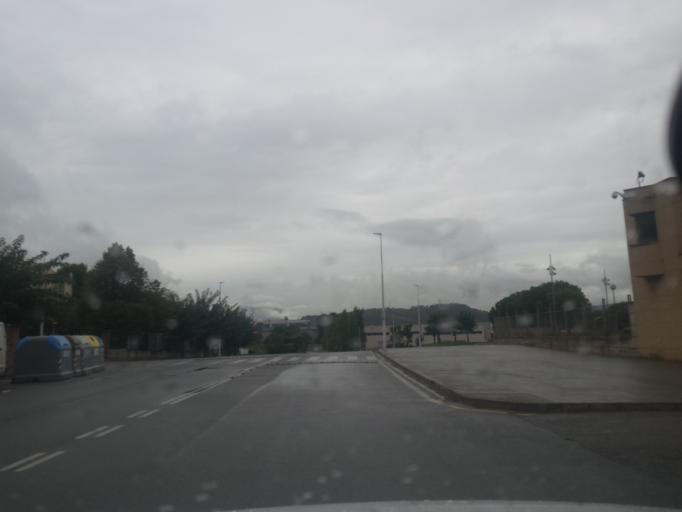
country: ES
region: Catalonia
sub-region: Provincia de Barcelona
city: Sant Andreu de la Barca
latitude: 41.4553
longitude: 1.9570
